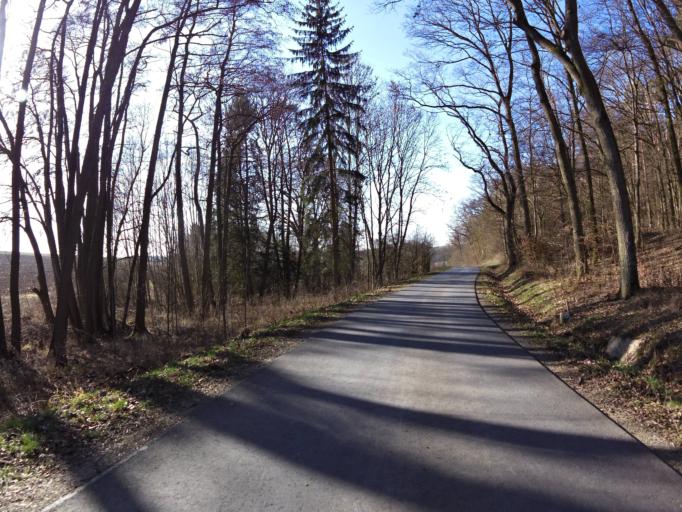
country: DE
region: Bavaria
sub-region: Regierungsbezirk Unterfranken
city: Estenfeld
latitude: 49.8498
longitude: 9.9887
